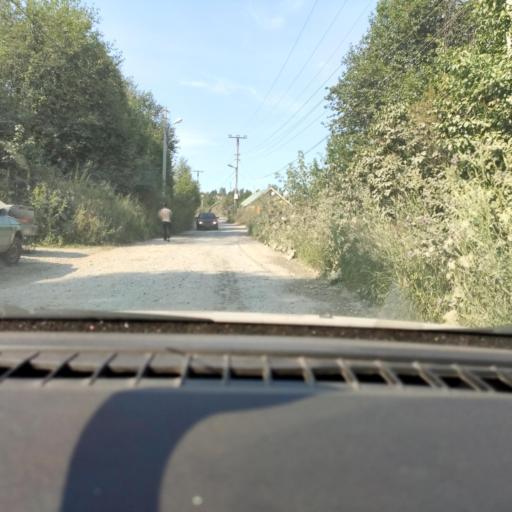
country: RU
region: Perm
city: Polazna
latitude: 58.1412
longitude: 56.4570
